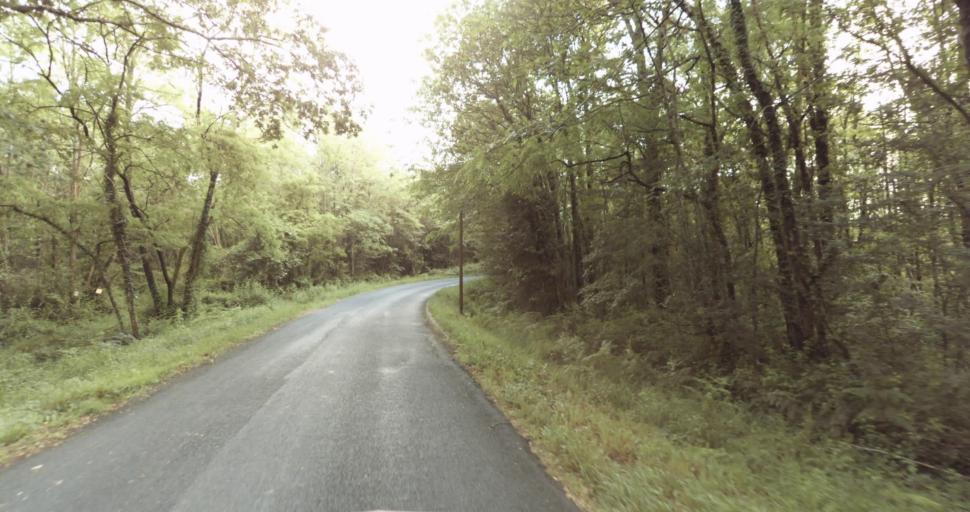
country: FR
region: Aquitaine
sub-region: Departement de la Dordogne
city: Le Bugue
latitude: 44.9313
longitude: 0.8184
